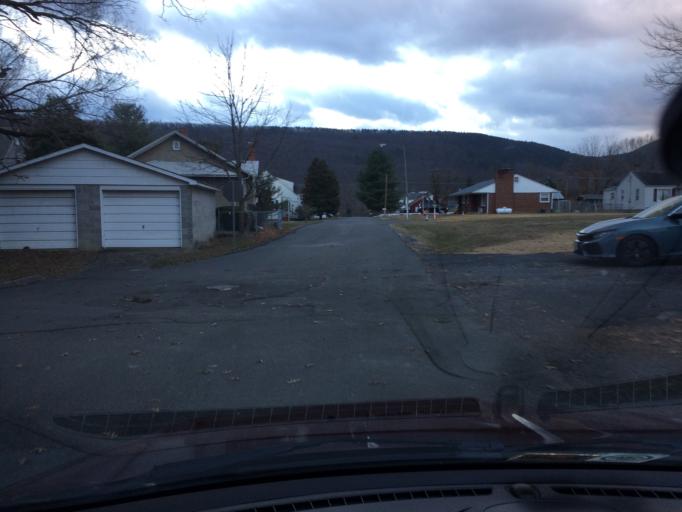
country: US
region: Virginia
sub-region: Alleghany County
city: Clifton Forge
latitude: 37.8183
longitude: -79.8130
